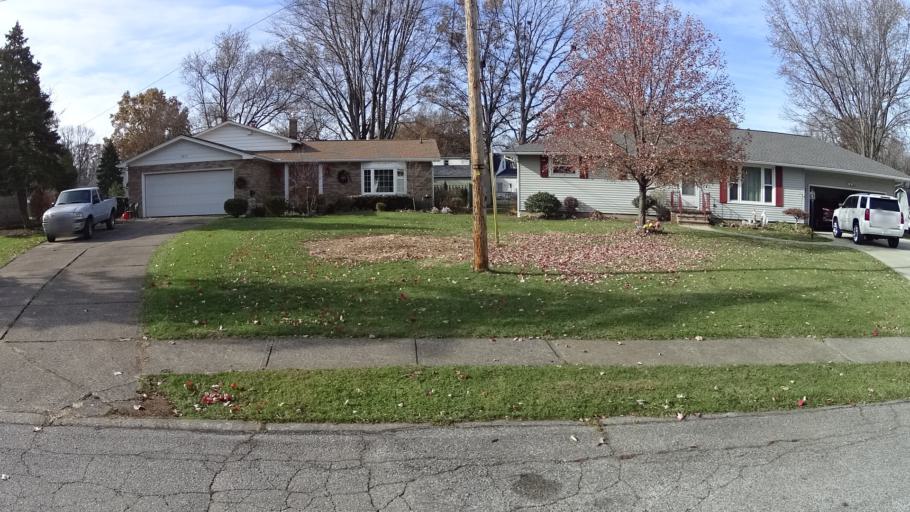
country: US
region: Ohio
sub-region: Lorain County
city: Sheffield
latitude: 41.3980
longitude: -82.0862
